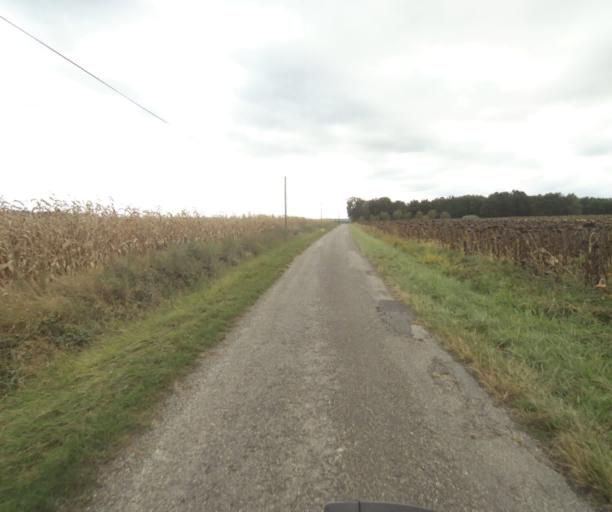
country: FR
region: Midi-Pyrenees
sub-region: Departement du Tarn-et-Garonne
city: Verdun-sur-Garonne
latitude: 43.8611
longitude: 1.1475
